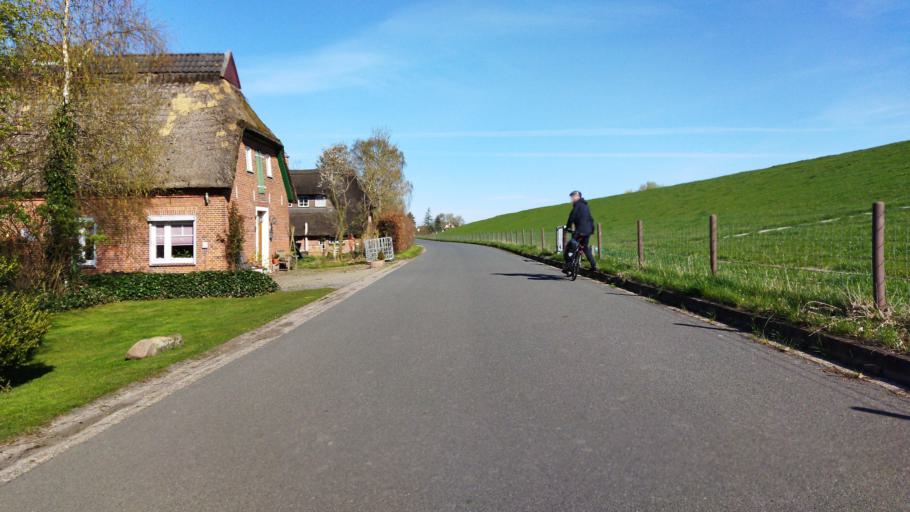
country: DE
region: Lower Saxony
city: Elsfleth
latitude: 53.2117
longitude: 8.4820
